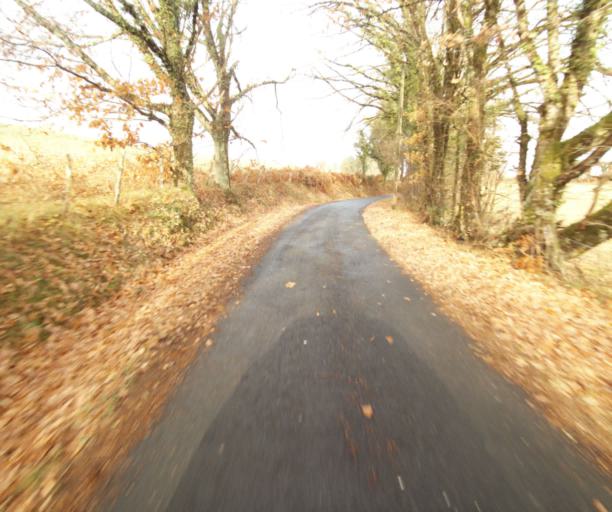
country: FR
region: Limousin
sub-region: Departement de la Correze
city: Saint-Mexant
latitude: 45.2614
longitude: 1.6385
